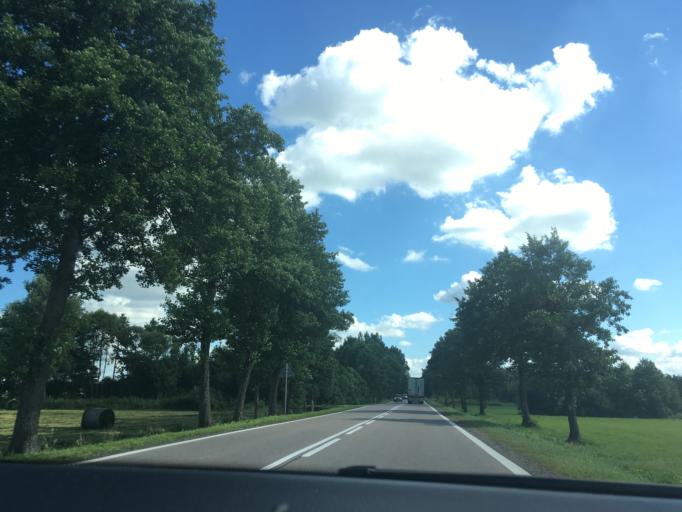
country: PL
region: Podlasie
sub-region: Powiat sokolski
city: Suchowola
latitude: 53.6684
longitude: 23.1215
